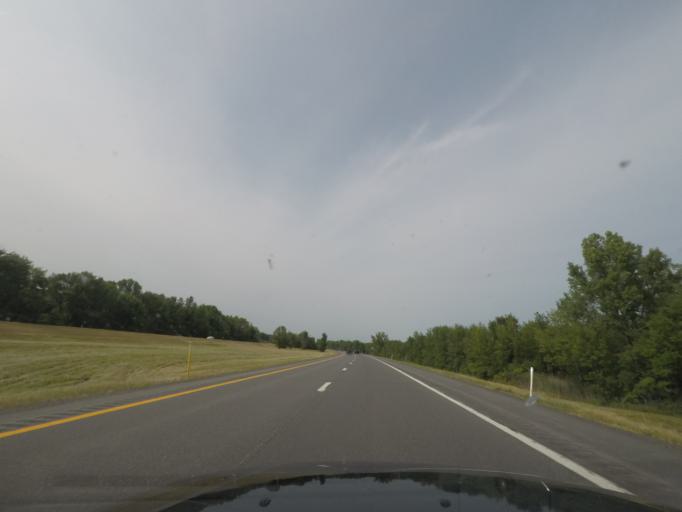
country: US
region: New York
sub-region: Essex County
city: Keeseville
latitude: 44.5268
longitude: -73.4965
